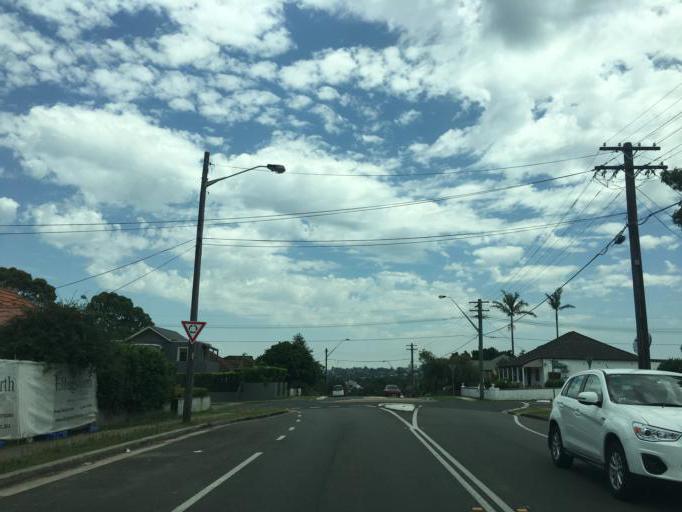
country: AU
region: New South Wales
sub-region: Hunters Hill
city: Gladesville
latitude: -33.8325
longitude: 151.1234
